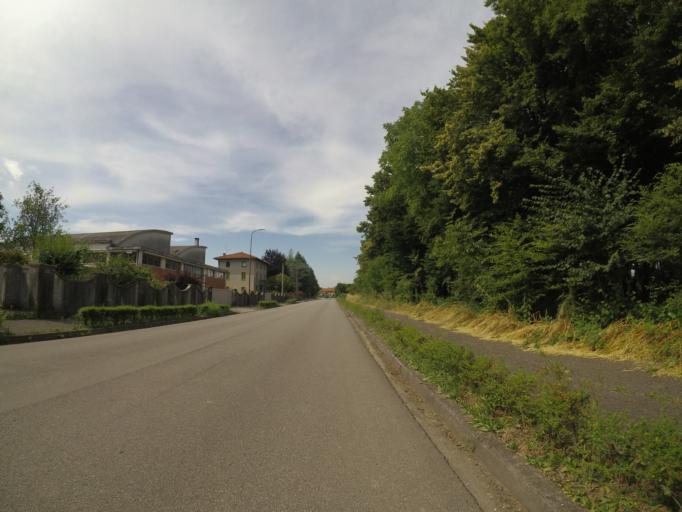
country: IT
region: Friuli Venezia Giulia
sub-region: Provincia di Udine
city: Camino al Tagliamento
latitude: 45.9301
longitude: 12.9448
